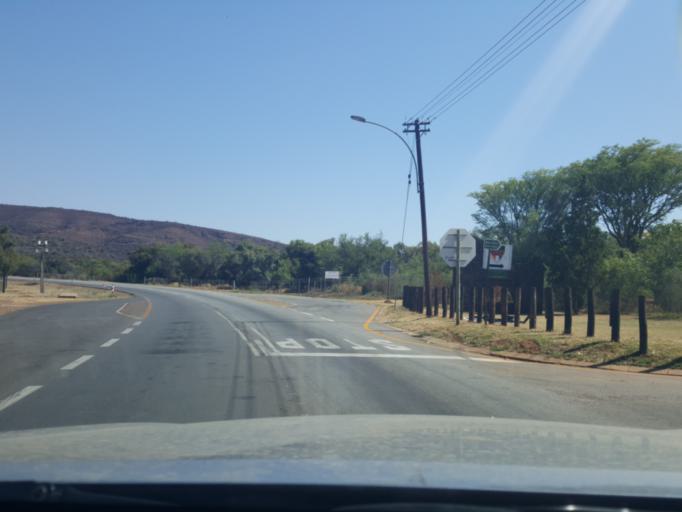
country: ZA
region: North-West
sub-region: Ngaka Modiri Molema District Municipality
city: Zeerust
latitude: -25.5257
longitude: 26.0746
